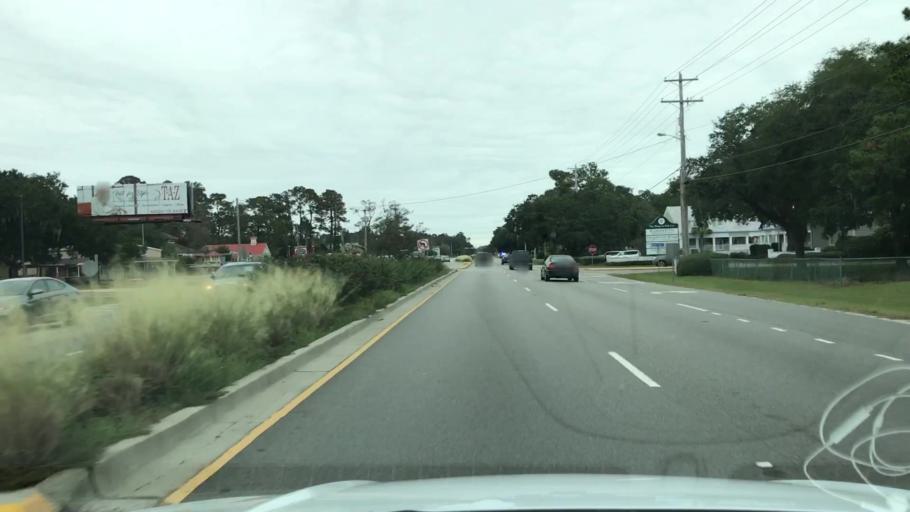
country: US
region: South Carolina
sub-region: Georgetown County
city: Murrells Inlet
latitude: 33.4455
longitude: -79.1223
